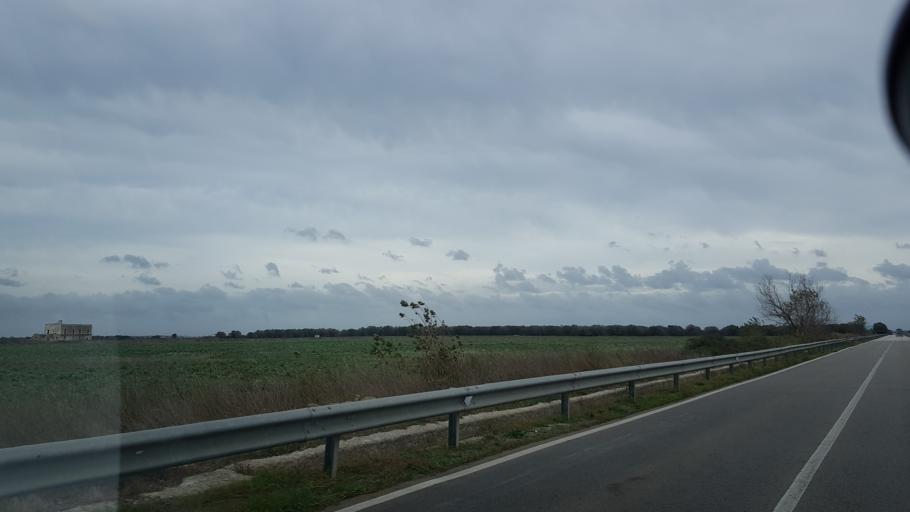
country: IT
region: Apulia
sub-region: Provincia di Brindisi
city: San Pancrazio Salentino
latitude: 40.4097
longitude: 17.8747
